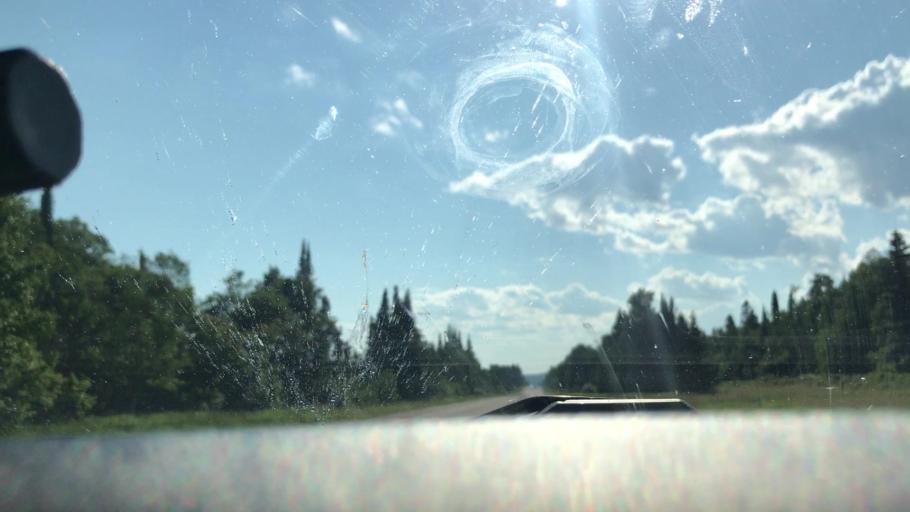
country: US
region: Minnesota
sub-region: Cook County
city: Grand Marais
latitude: 47.7972
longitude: -90.1147
